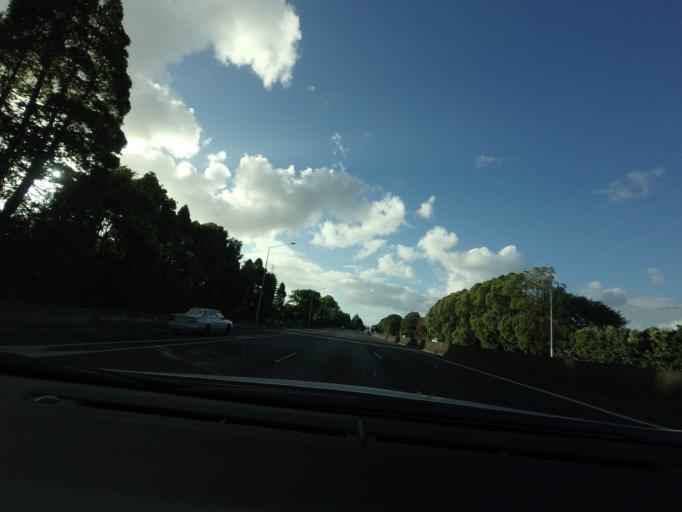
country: NZ
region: Auckland
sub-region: Auckland
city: Manukau City
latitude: -36.9623
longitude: 174.8655
